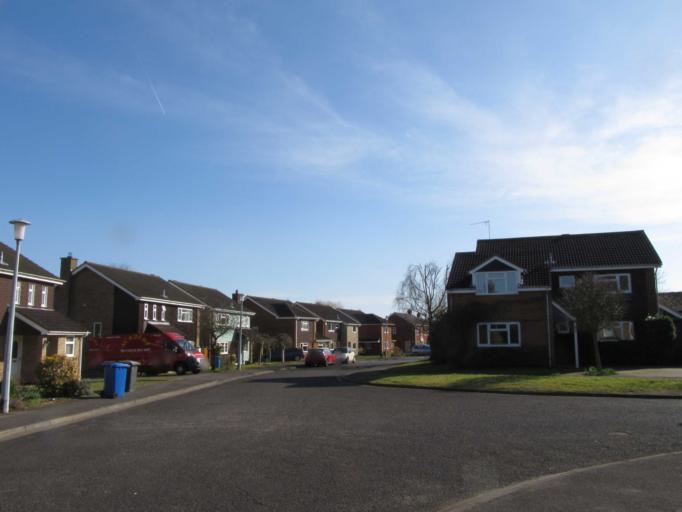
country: GB
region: England
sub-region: Royal Borough of Windsor and Maidenhead
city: Maidenhead
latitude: 51.5356
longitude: -0.7434
